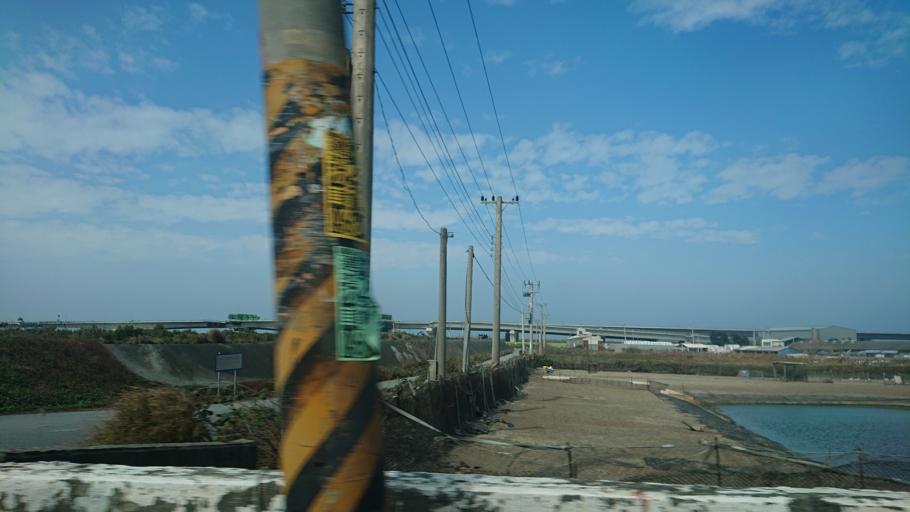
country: TW
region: Taiwan
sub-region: Changhua
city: Chang-hua
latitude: 23.9346
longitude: 120.3234
